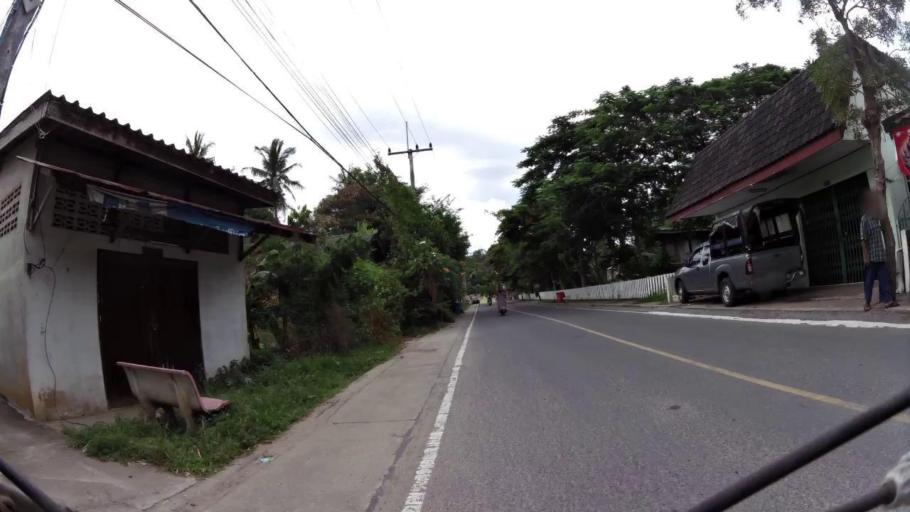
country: TH
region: Prachuap Khiri Khan
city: Prachuap Khiri Khan
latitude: 11.7495
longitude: 99.7899
